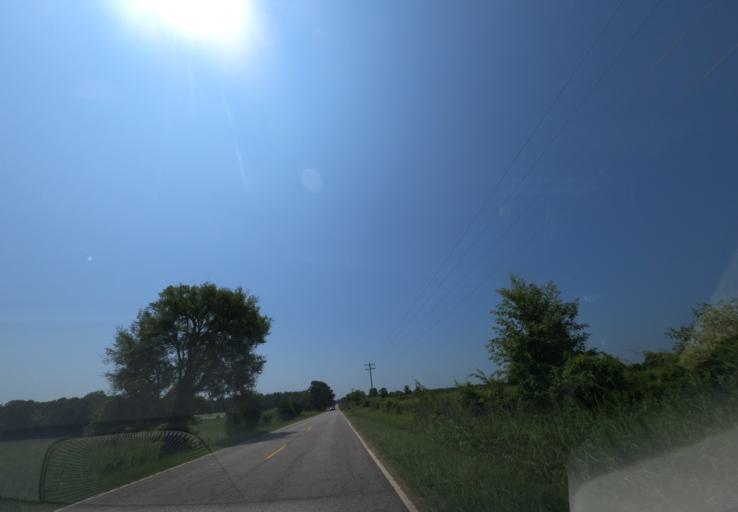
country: US
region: South Carolina
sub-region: Greenwood County
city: Greenwood
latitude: 34.0272
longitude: -82.1286
